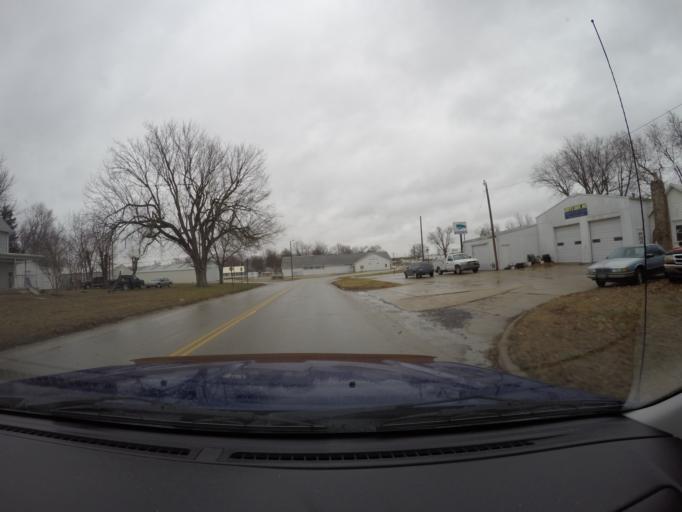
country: US
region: Kansas
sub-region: Jackson County
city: Holton
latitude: 39.4634
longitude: -95.7303
